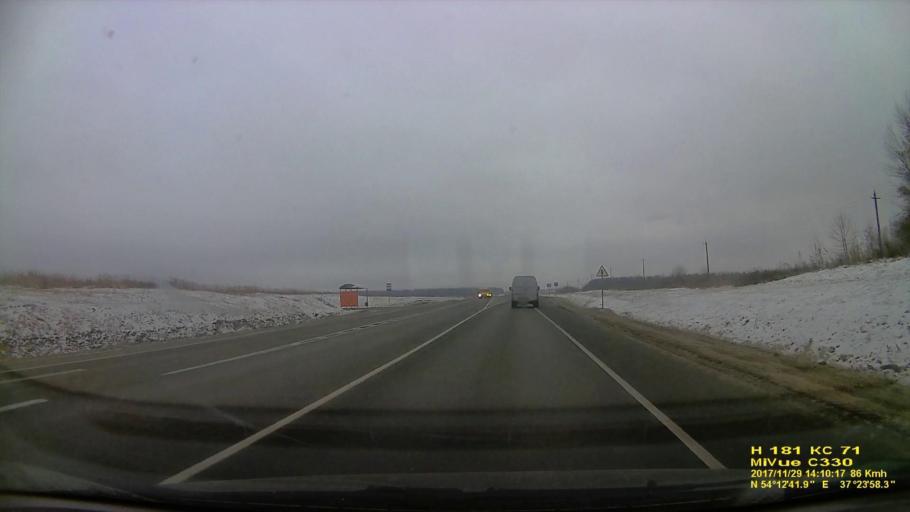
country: RU
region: Tula
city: Leninskiy
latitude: 54.2115
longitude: 37.3997
